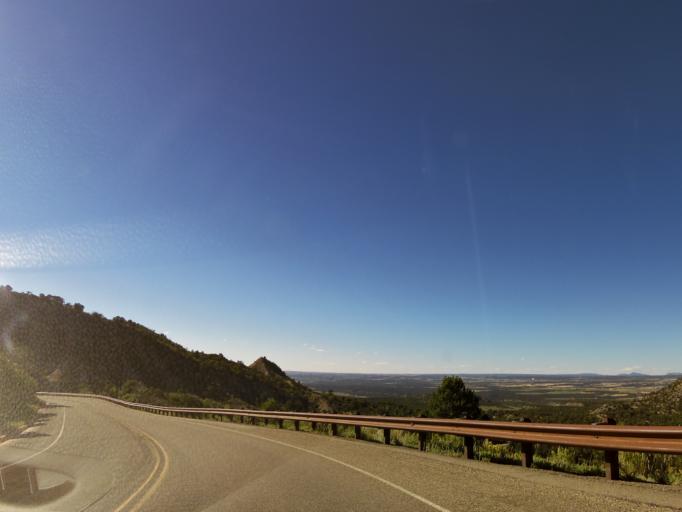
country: US
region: Colorado
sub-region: Montezuma County
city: Mancos
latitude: 37.3222
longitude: -108.4150
